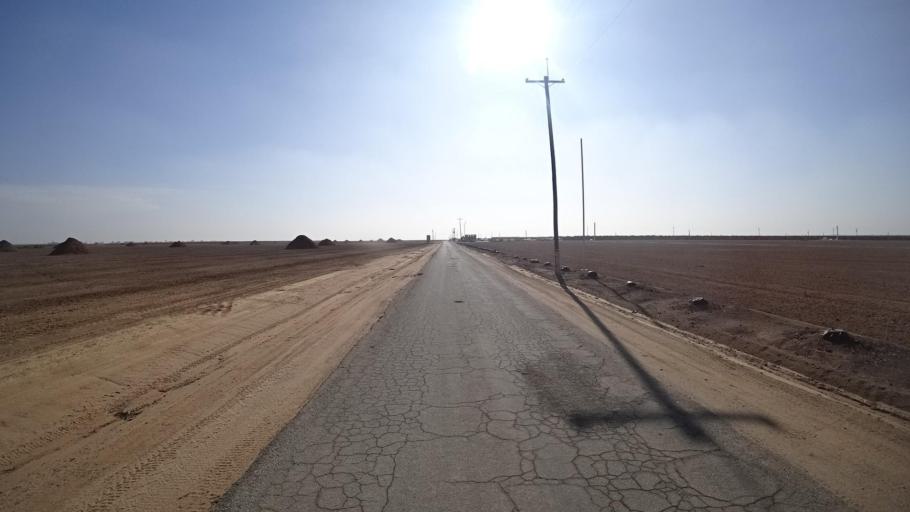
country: US
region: California
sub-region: Kern County
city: Shafter
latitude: 35.5394
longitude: -119.1336
